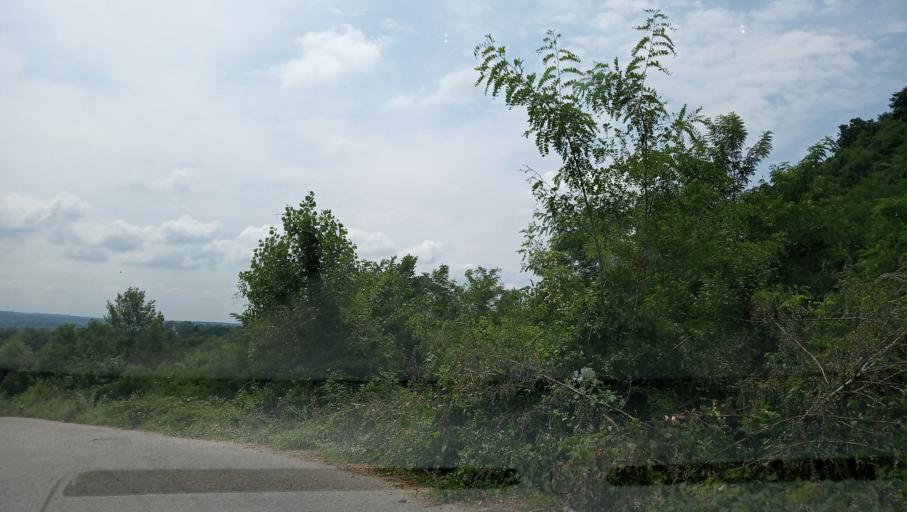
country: RO
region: Gorj
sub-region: Comuna Turcinesti
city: Turcinesti
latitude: 45.1421
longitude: 23.3424
